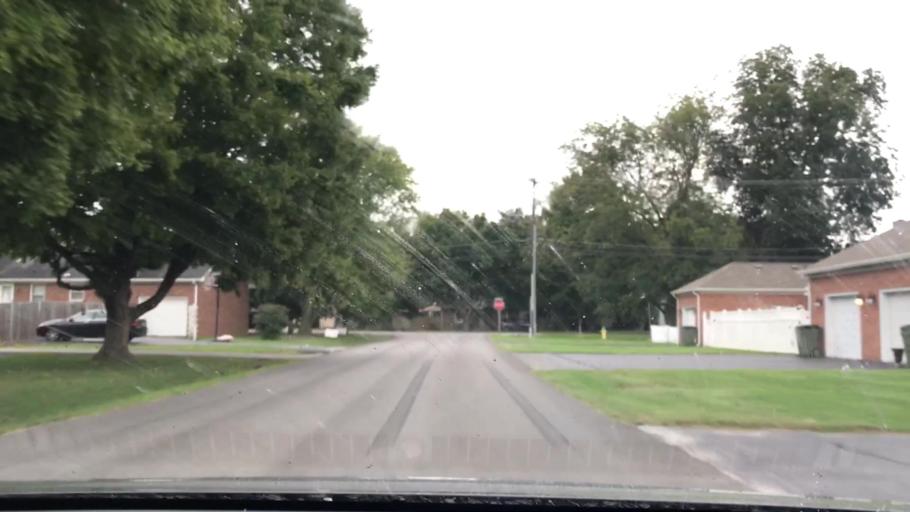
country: US
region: Kentucky
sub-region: Christian County
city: Hopkinsville
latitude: 36.8551
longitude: -87.5022
